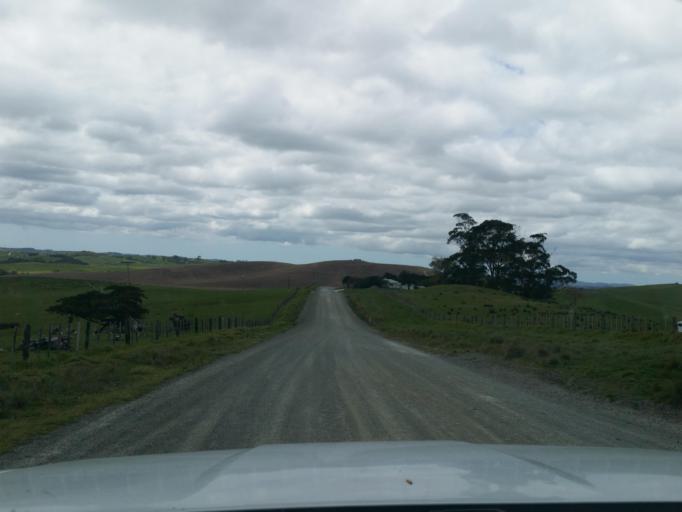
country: NZ
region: Auckland
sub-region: Auckland
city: Wellsford
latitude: -36.2878
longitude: 174.3377
